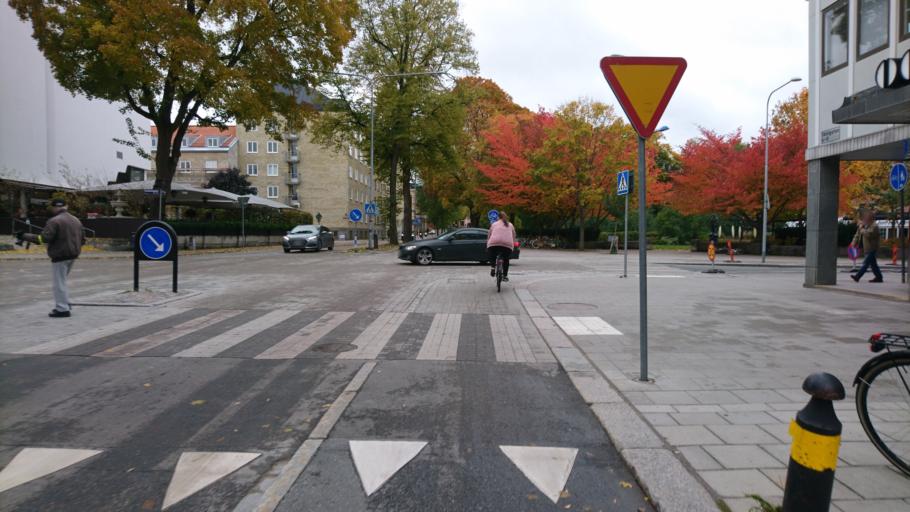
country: SE
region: Uppsala
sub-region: Uppsala Kommun
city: Uppsala
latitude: 59.8607
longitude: 17.6286
